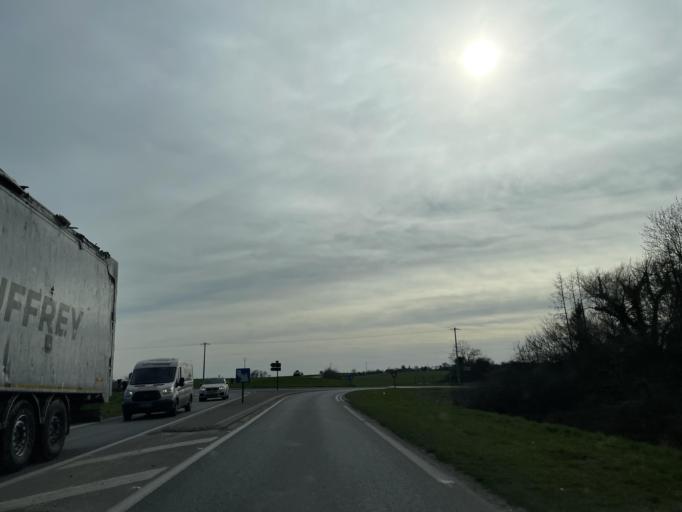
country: FR
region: Ile-de-France
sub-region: Departement de Seine-et-Marne
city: Jouy-le-Chatel
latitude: 48.6694
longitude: 3.1307
